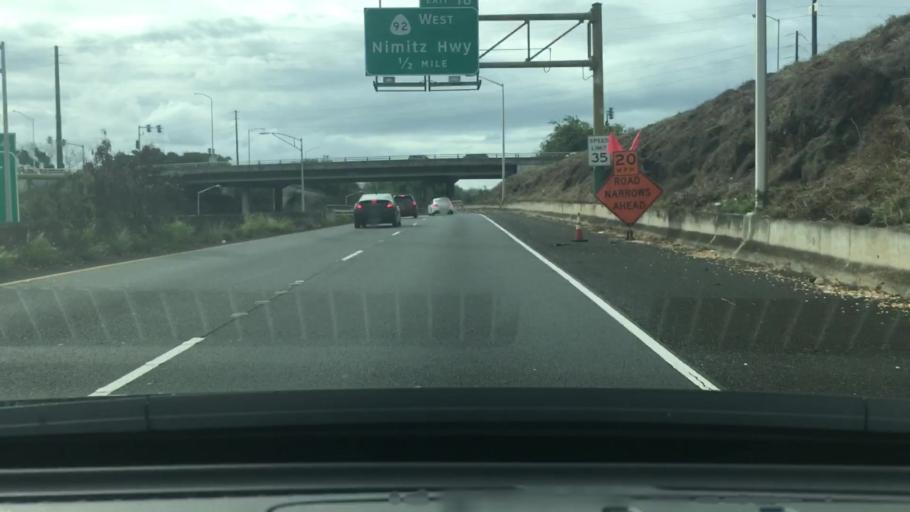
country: US
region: Hawaii
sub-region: Honolulu County
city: Honolulu
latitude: 21.3372
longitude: -157.8829
